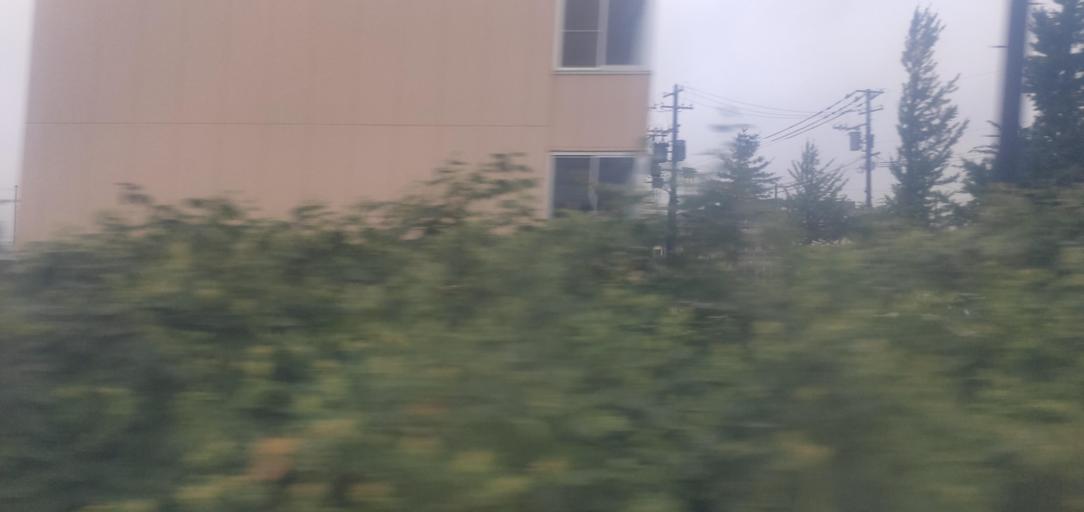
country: JP
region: Hokkaido
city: Kitahiroshima
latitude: 42.8845
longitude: 141.5844
